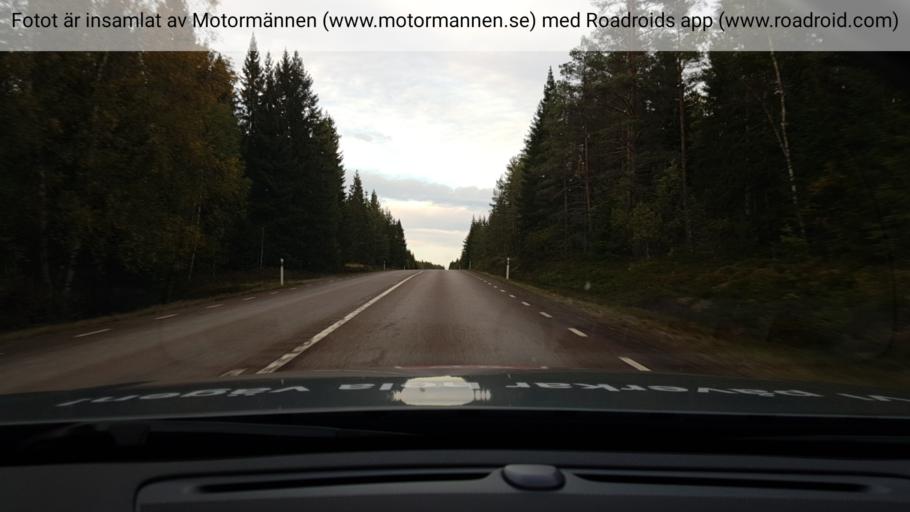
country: SE
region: Vaestra Goetaland
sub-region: Amals Kommun
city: Amal
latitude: 59.0603
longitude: 12.5388
